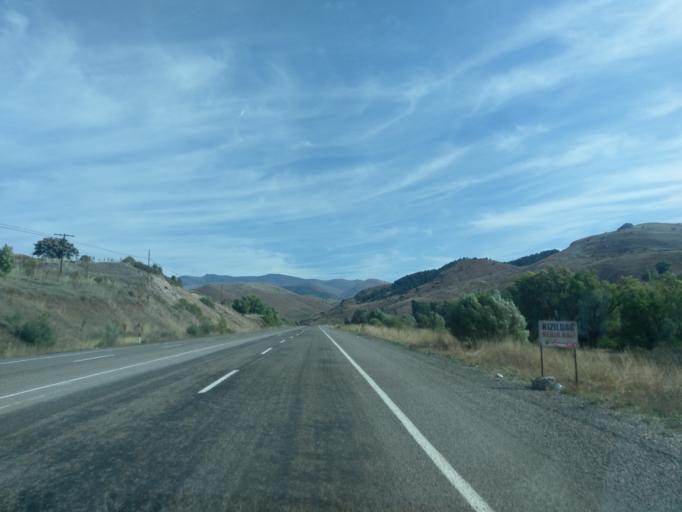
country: TR
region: Sivas
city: Imranli
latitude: 39.8439
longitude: 38.2876
